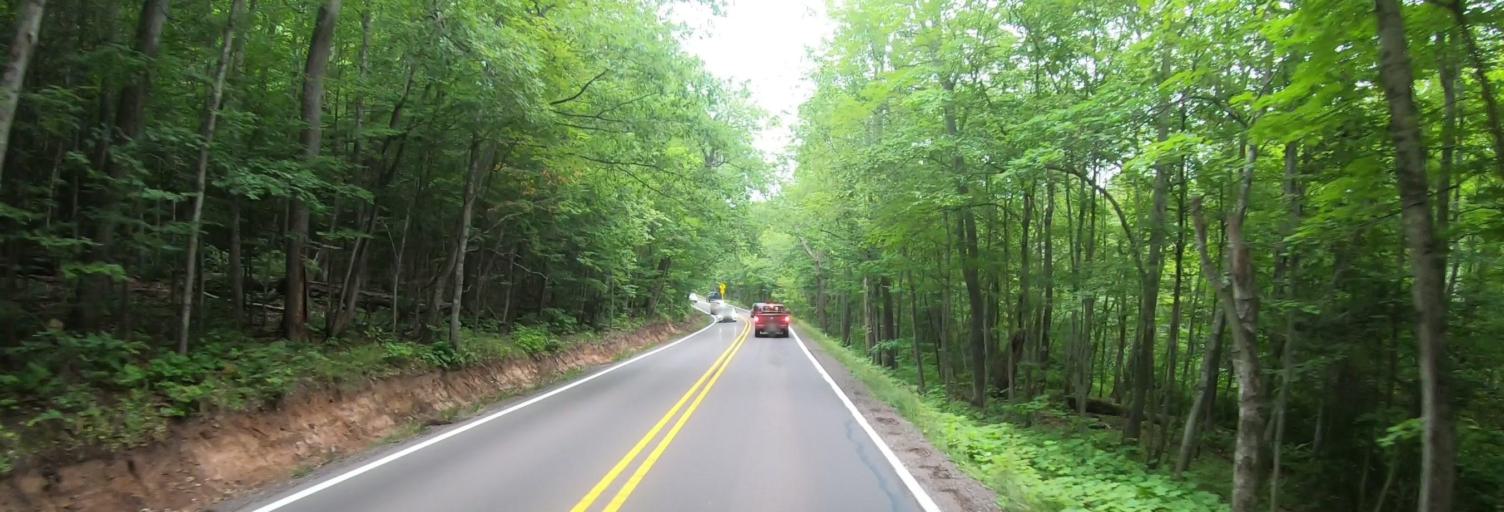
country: US
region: Michigan
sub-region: Keweenaw County
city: Eagle River
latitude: 47.4277
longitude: -87.9886
